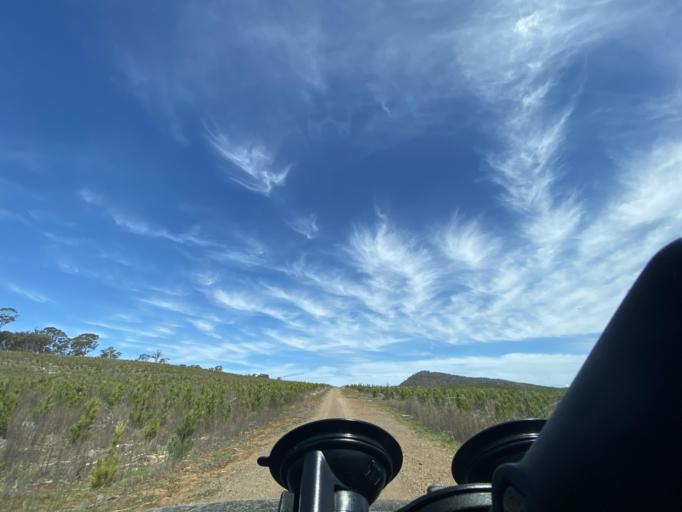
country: AU
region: Victoria
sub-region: Mansfield
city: Mansfield
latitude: -36.8202
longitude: 146.1025
